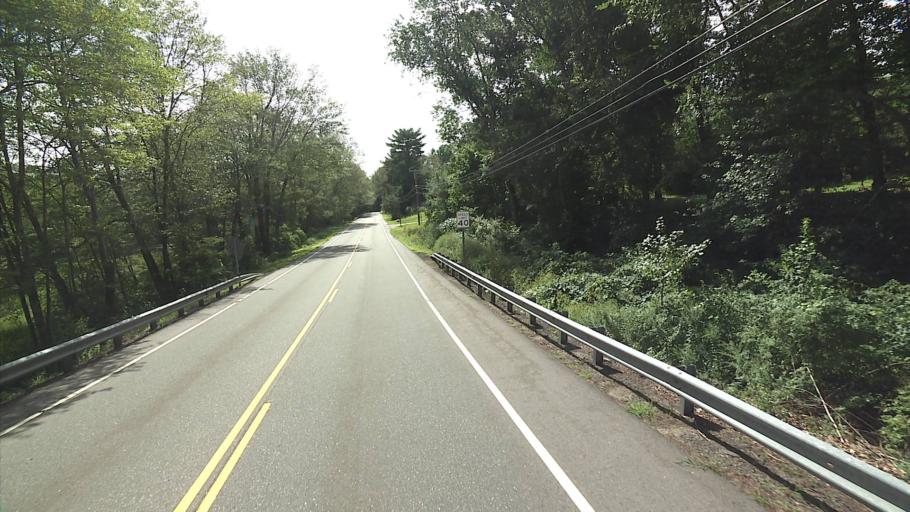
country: US
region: Connecticut
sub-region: Windham County
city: South Woodstock
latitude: 41.9352
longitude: -72.0940
